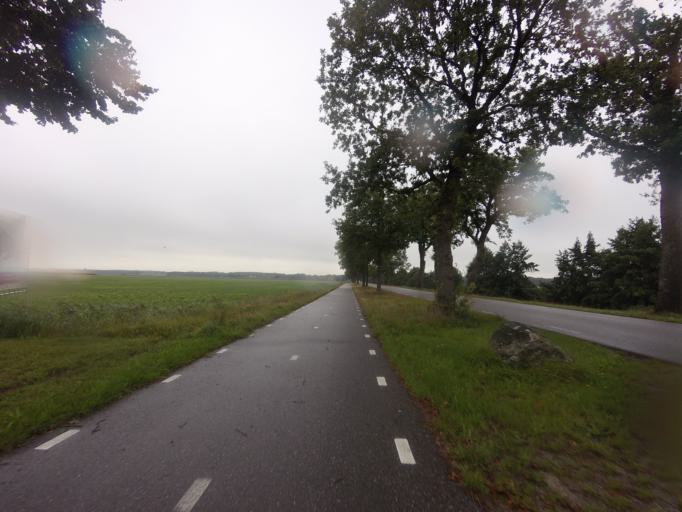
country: NL
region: Friesland
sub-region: Gemeente Heerenveen
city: Nieuwehorne
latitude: 52.9455
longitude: 6.1176
